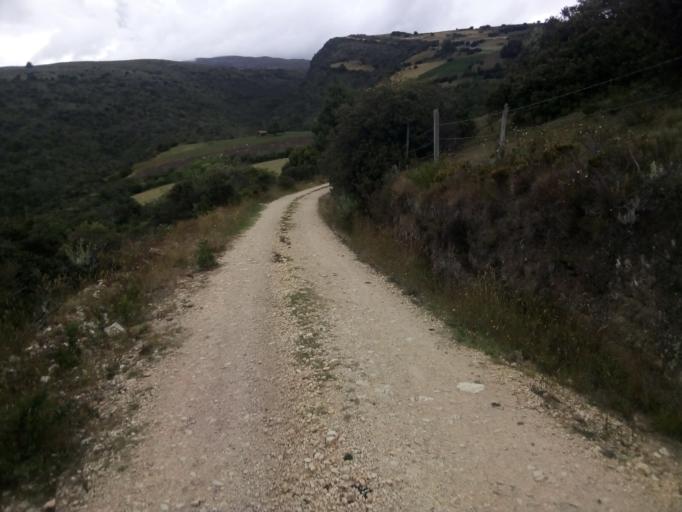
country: CO
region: Boyaca
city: Toca
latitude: 5.5875
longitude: -73.1285
